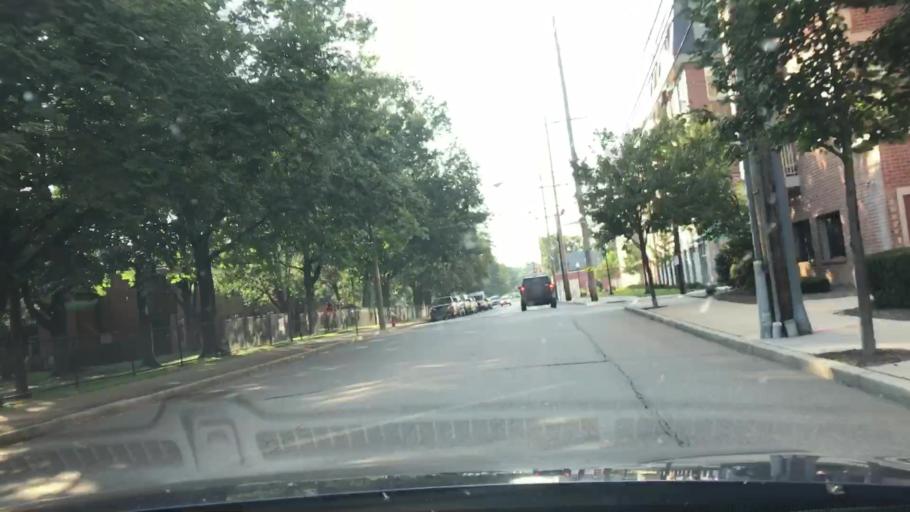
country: US
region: New Jersey
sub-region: Bergen County
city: Englewood
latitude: 40.8933
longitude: -73.9772
